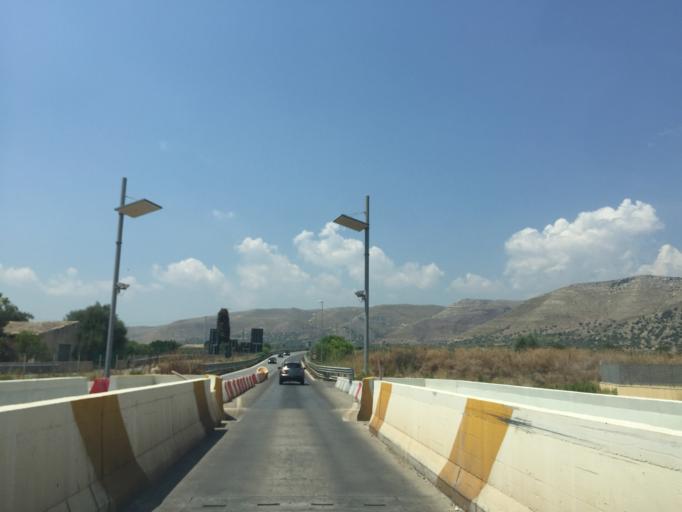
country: IT
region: Sicily
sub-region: Provincia di Siracusa
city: Avola
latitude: 36.9315
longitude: 15.1612
